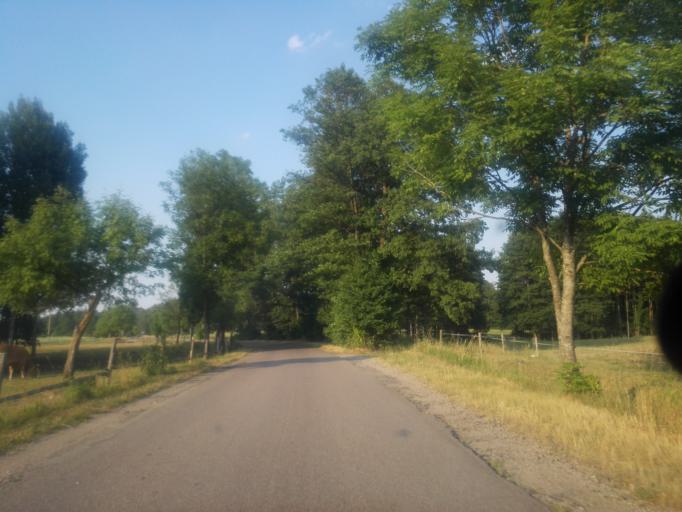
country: PL
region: Podlasie
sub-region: Suwalki
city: Suwalki
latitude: 54.0690
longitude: 22.9970
